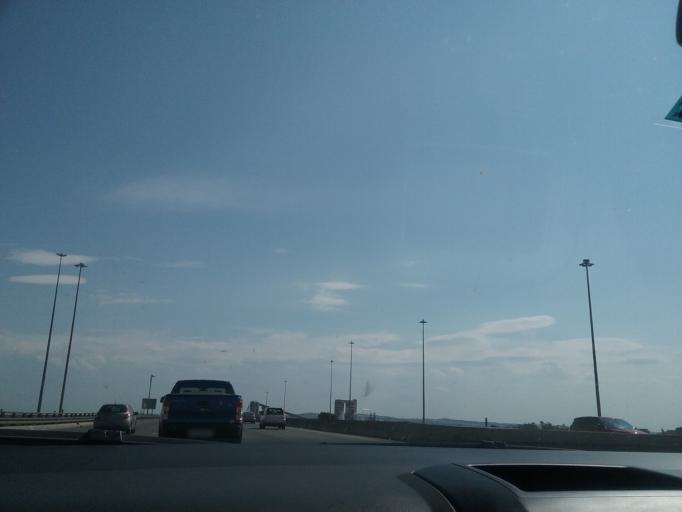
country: ZA
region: Gauteng
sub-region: Ekurhuleni Metropolitan Municipality
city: Germiston
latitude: -26.2136
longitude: 28.1337
